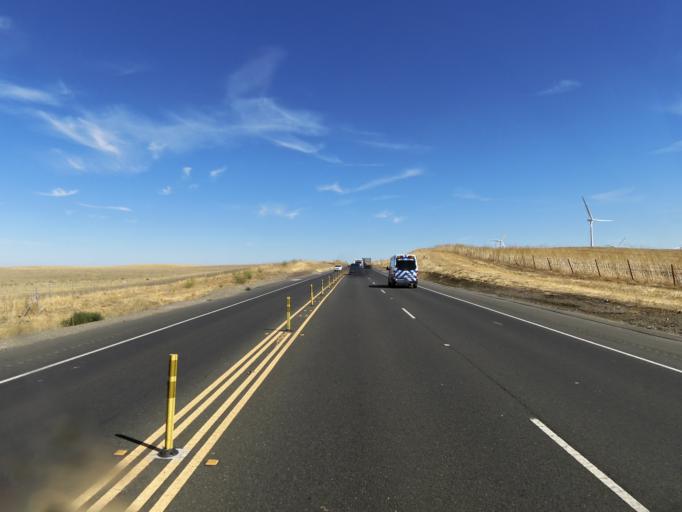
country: US
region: California
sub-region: Solano County
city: Rio Vista
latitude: 38.1835
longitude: -121.8022
